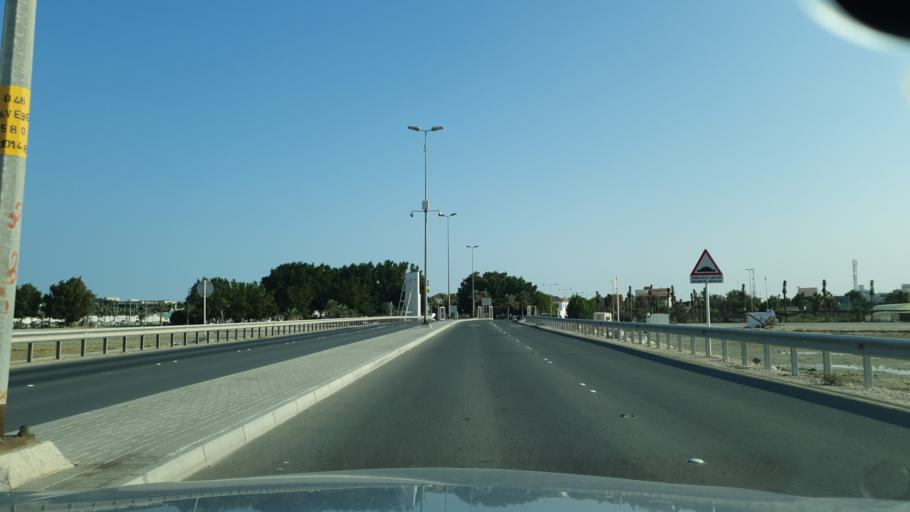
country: BH
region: Manama
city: Jidd Hafs
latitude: 26.2255
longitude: 50.4584
